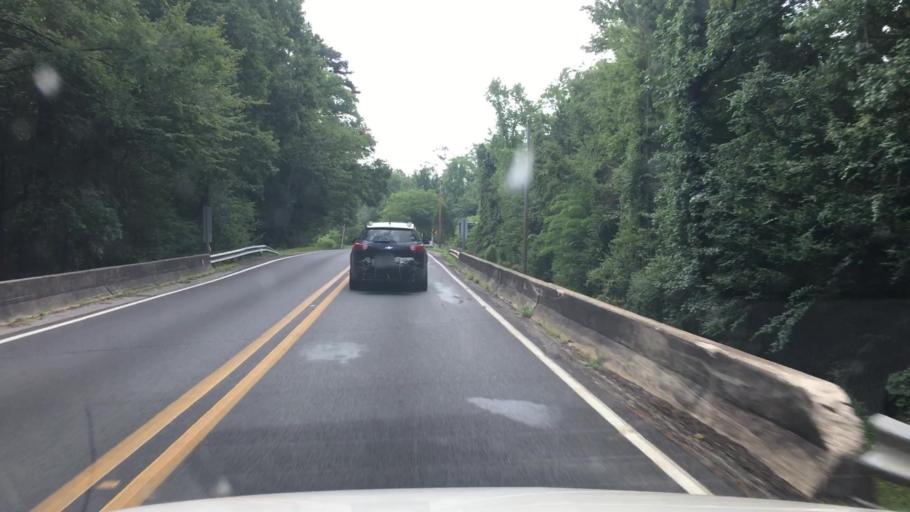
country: US
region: Arkansas
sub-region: Garland County
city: Lake Hamilton
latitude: 34.3412
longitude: -93.1837
